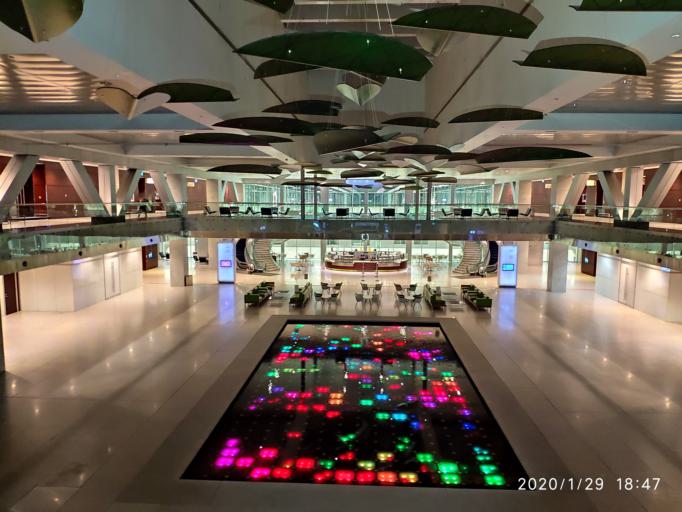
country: QA
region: Baladiyat ar Rayyan
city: Ar Rayyan
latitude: 25.3221
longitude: 51.4373
